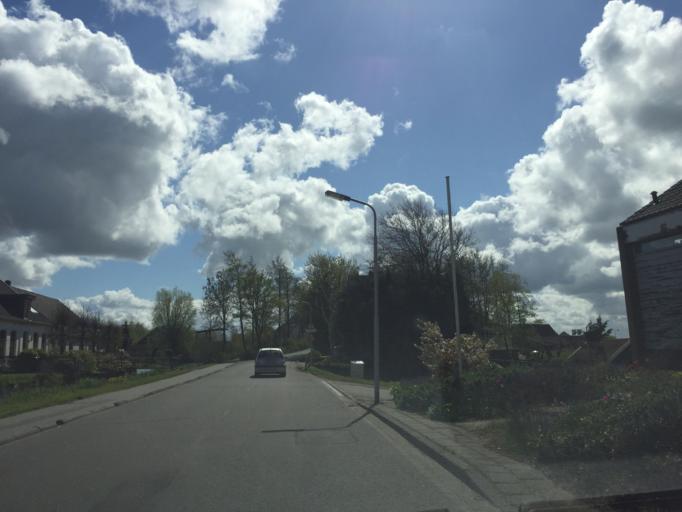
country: NL
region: South Holland
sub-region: Gemeente Kaag en Braassem
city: Oude Wetering
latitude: 52.2131
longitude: 4.6202
